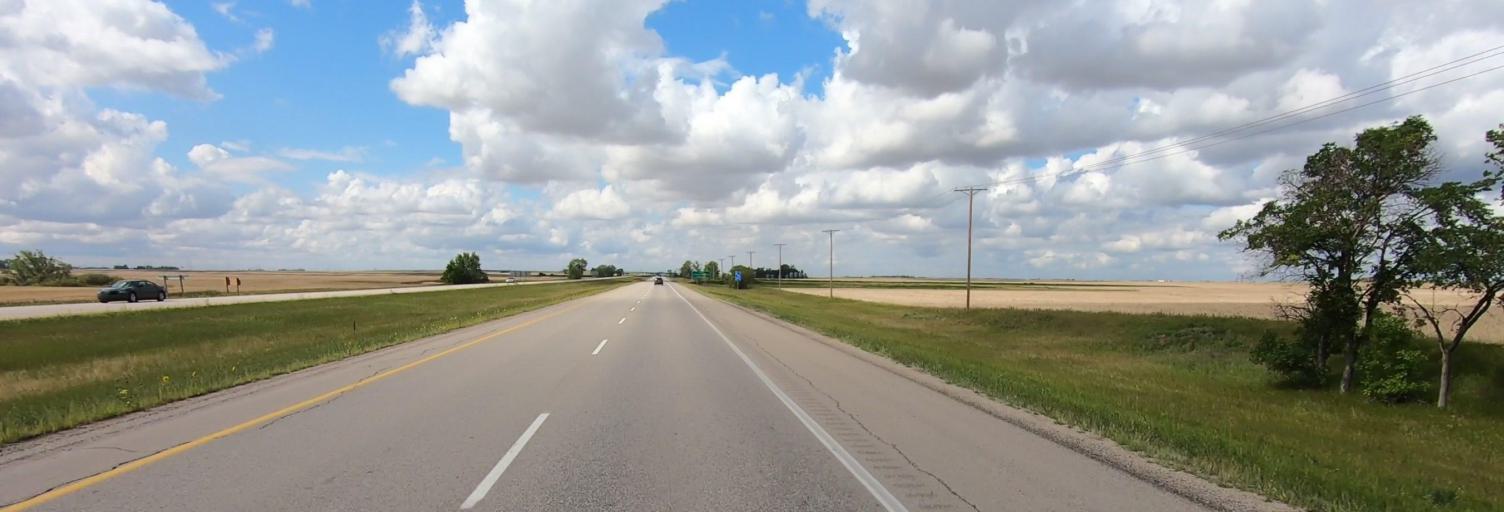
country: CA
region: Saskatchewan
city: Regina
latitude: 50.3969
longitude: -104.6668
